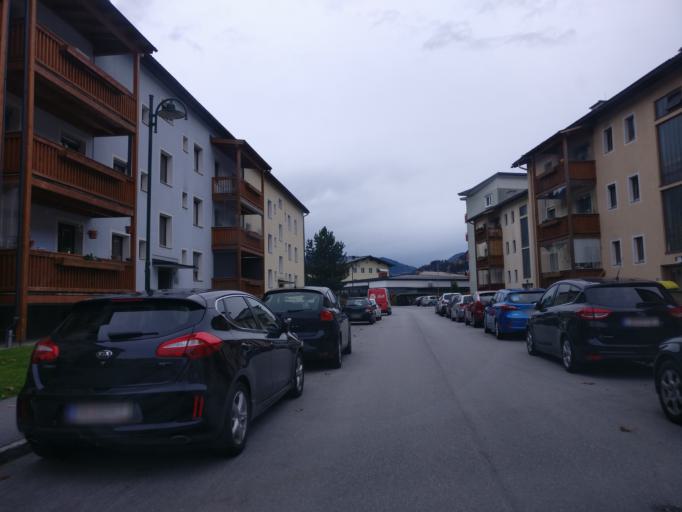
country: AT
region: Salzburg
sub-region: Politischer Bezirk Sankt Johann im Pongau
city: Bischofshofen
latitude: 47.4248
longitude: 13.2158
